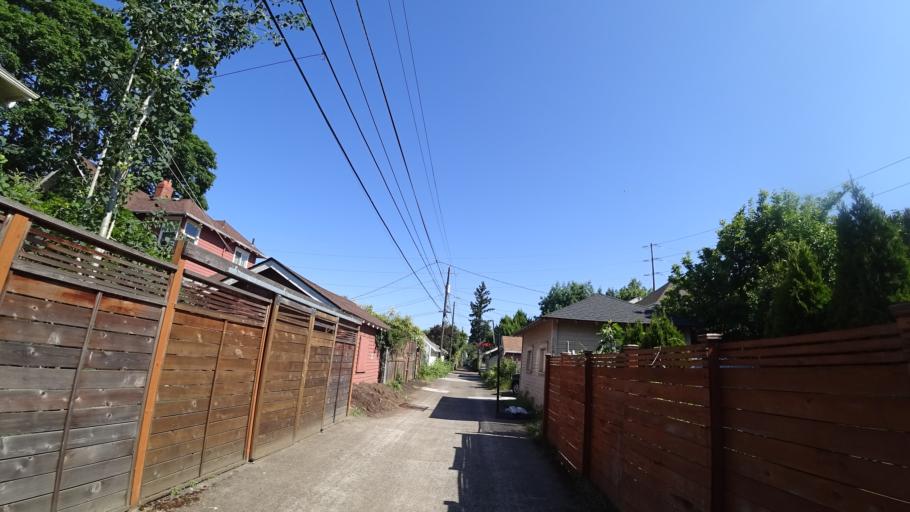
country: US
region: Oregon
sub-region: Multnomah County
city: Portland
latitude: 45.5610
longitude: -122.6643
